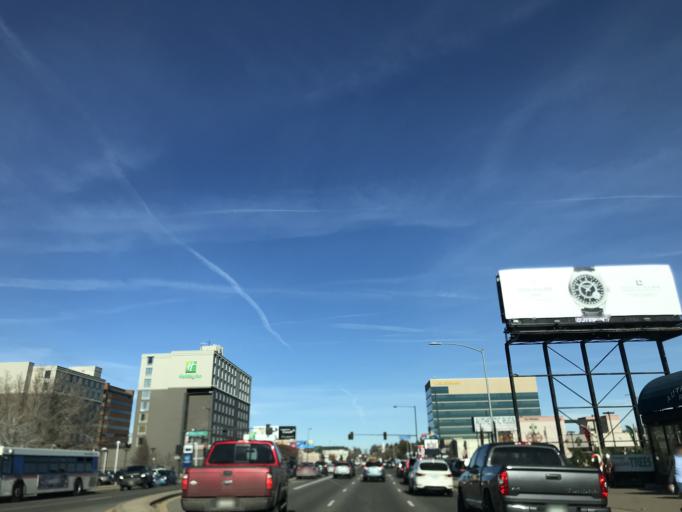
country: US
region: Colorado
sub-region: Arapahoe County
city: Glendale
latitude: 39.7066
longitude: -104.9407
